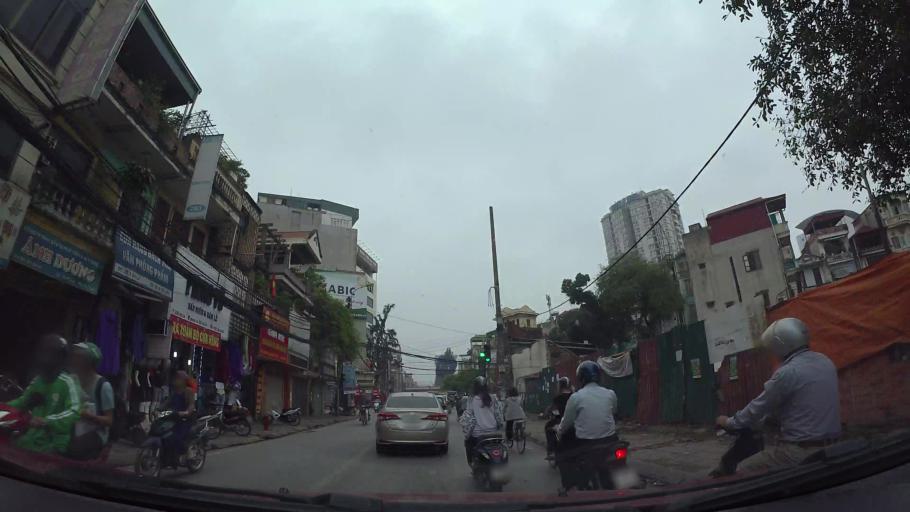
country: VN
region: Ha Noi
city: Hai BaTrung
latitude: 20.9972
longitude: 105.8432
